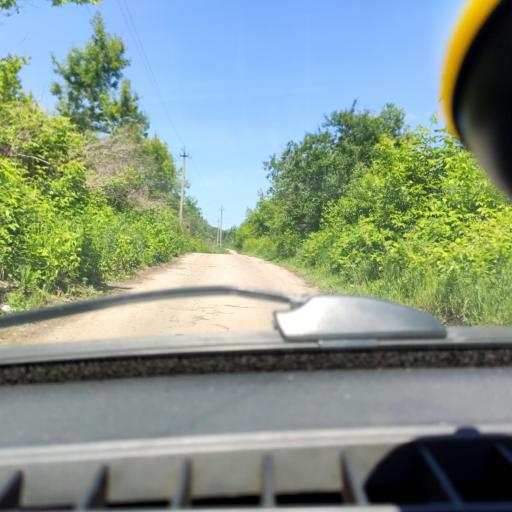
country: RU
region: Samara
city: Zhigulevsk
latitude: 53.3792
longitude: 49.5084
